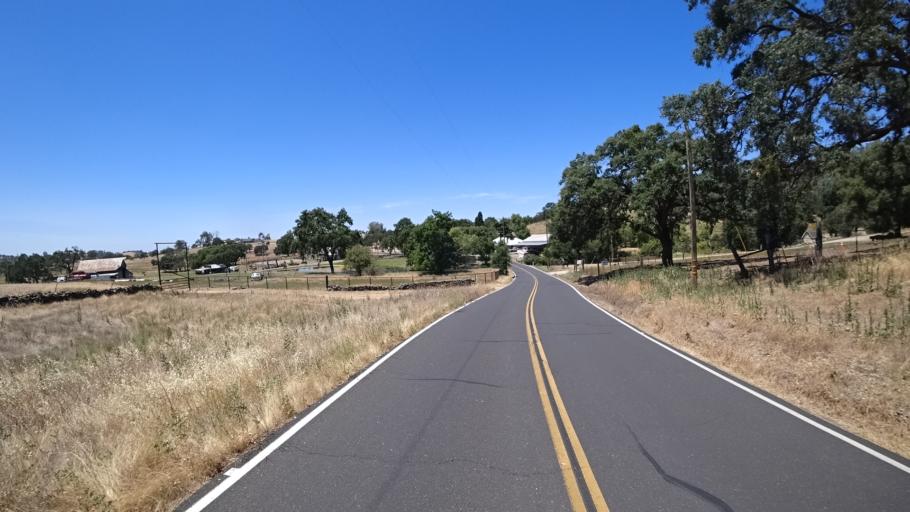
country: US
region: California
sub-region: Calaveras County
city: Valley Springs
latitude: 38.2335
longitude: -120.8083
